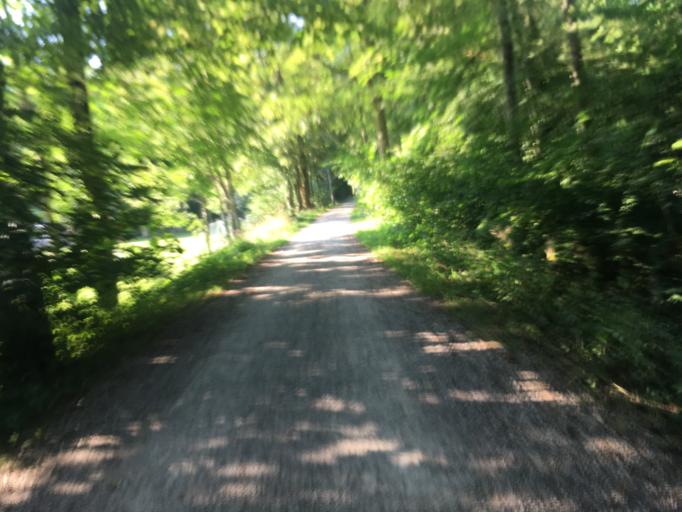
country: CH
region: Bern
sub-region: Emmental District
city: Oberburg
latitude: 47.0387
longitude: 7.6336
